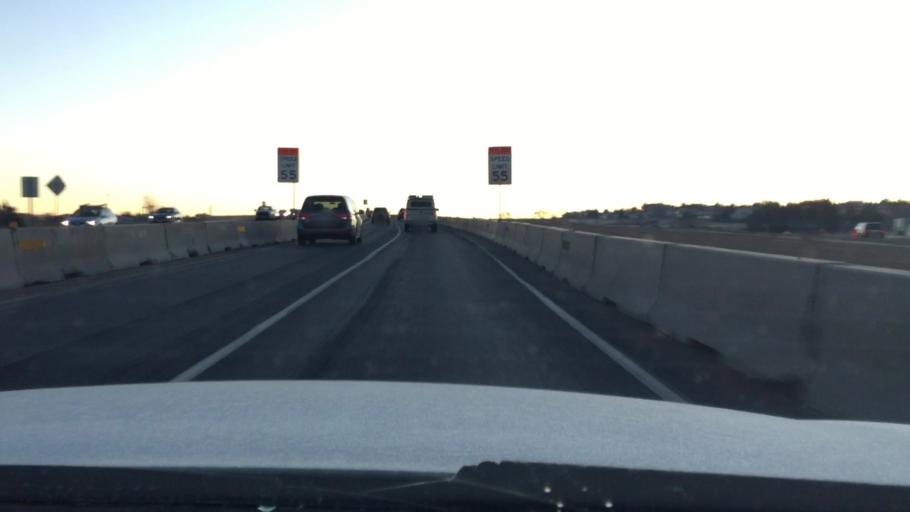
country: US
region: Colorado
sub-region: Douglas County
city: Highlands Ranch
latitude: 39.5635
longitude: -104.9638
